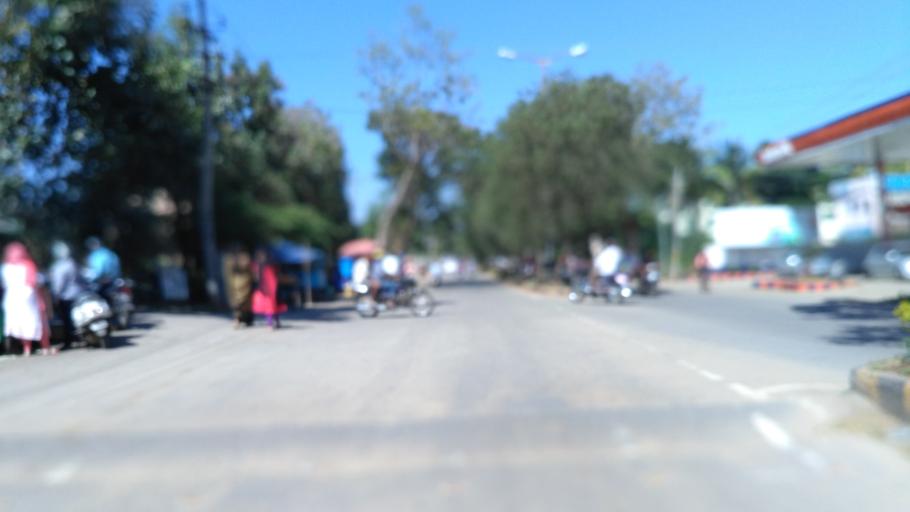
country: IN
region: Karnataka
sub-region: Hassan
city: Hassan
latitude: 13.0132
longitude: 76.1059
